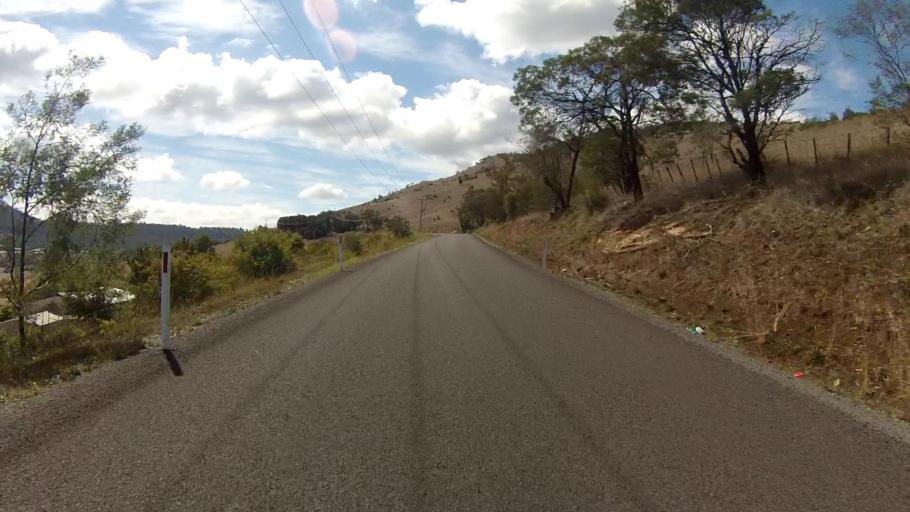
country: AU
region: Tasmania
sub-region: Glenorchy
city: Austins Ferry
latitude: -42.7285
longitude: 147.2721
